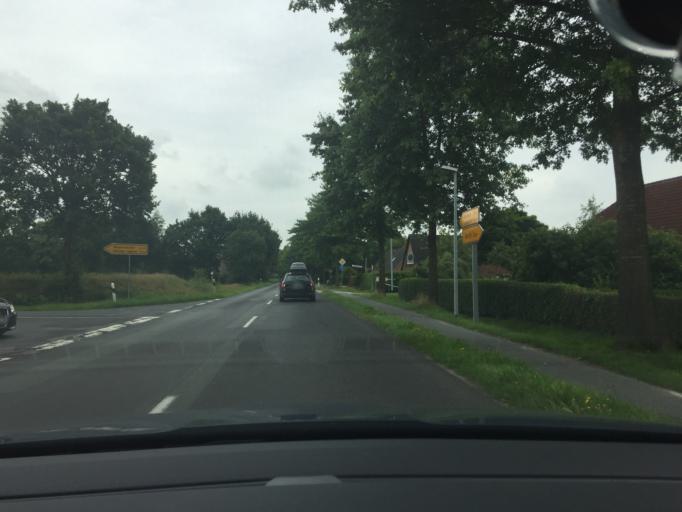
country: DE
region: Lower Saxony
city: Aurich
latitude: 53.4404
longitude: 7.4763
